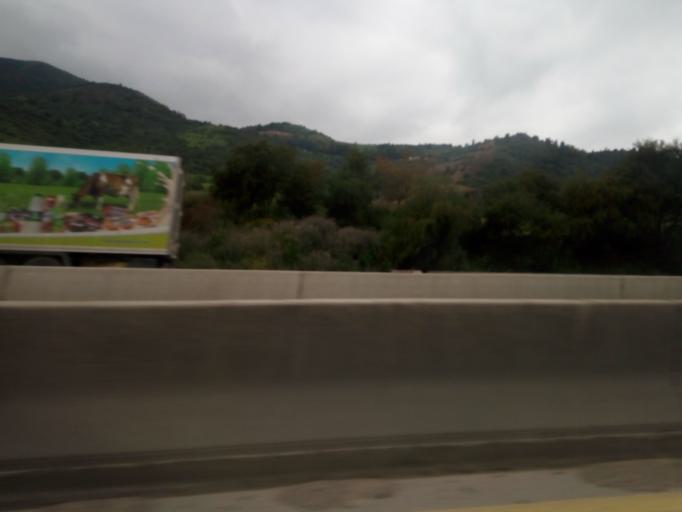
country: DZ
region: Bouira
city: Lakhdaria
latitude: 36.5617
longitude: 3.5738
